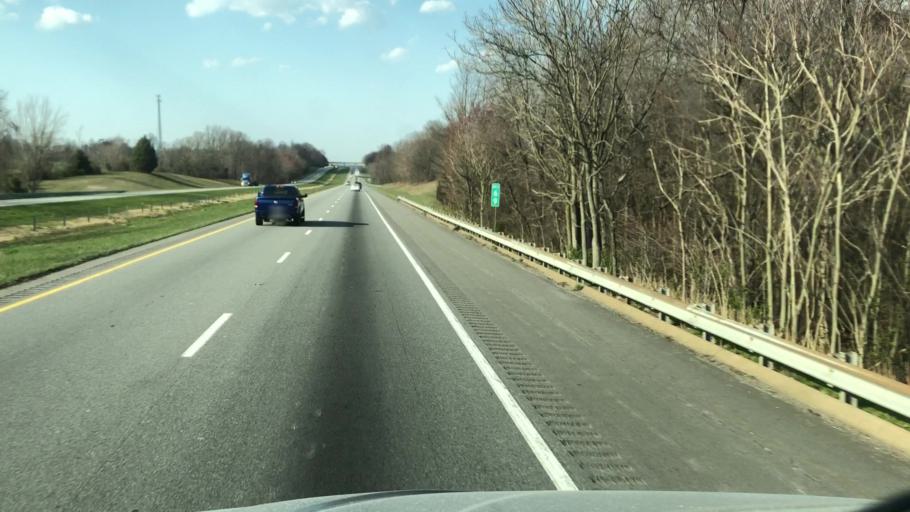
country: US
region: North Carolina
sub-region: Yadkin County
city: Yadkinville
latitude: 36.0578
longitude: -80.8225
